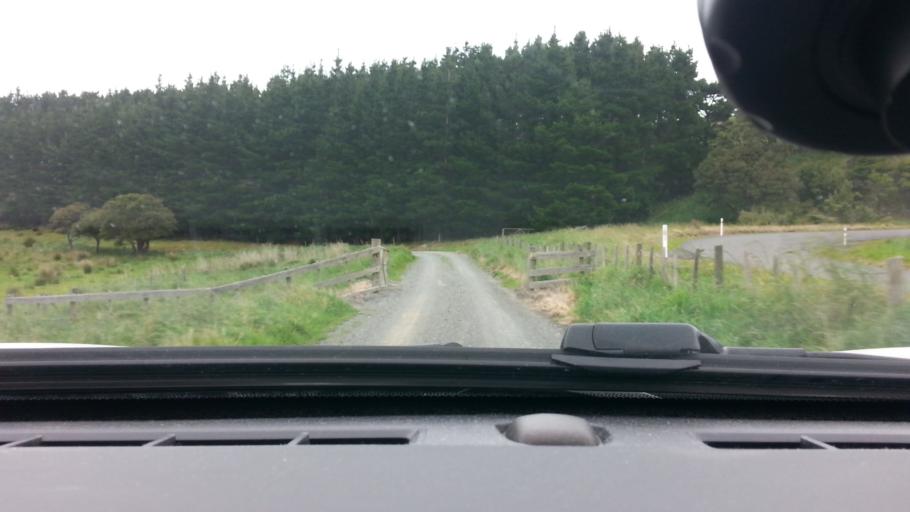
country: NZ
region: Wellington
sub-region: Upper Hutt City
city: Upper Hutt
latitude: -41.3741
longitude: 175.1038
